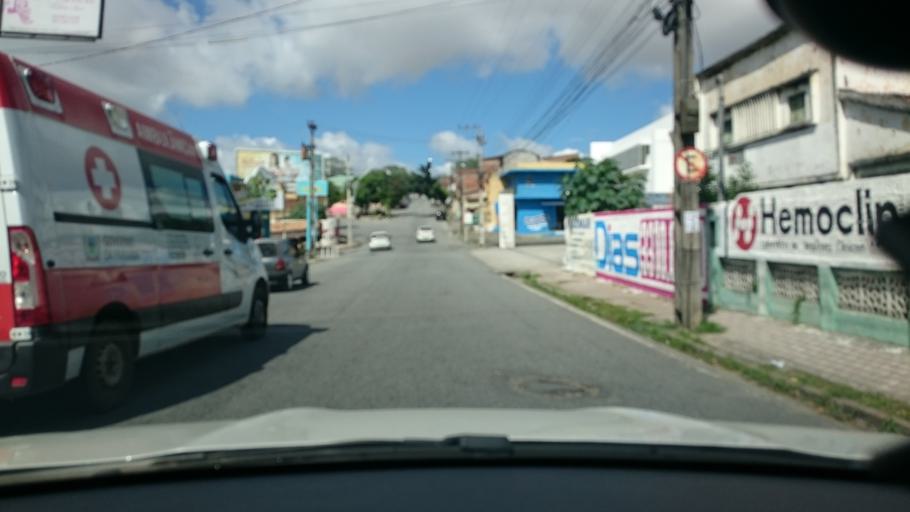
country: BR
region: Paraiba
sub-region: Campina Grande
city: Campina Grande
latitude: -7.2217
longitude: -35.8927
